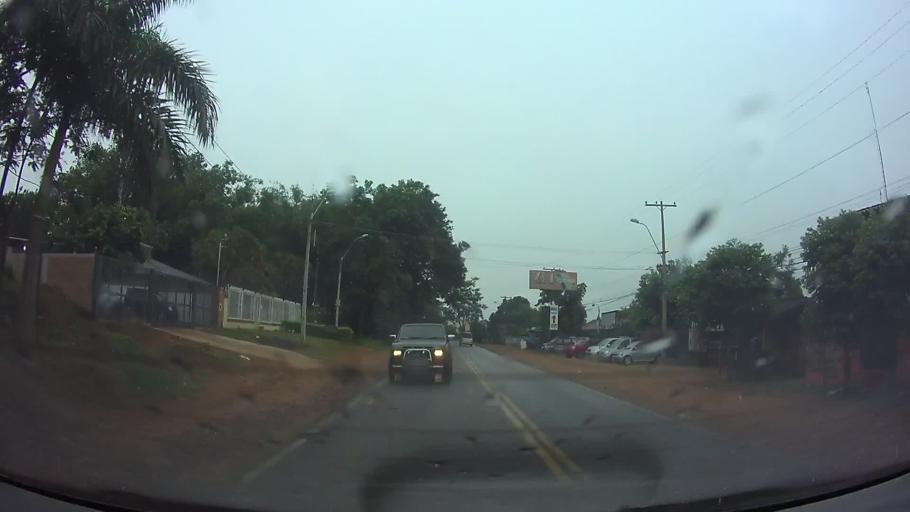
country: PY
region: Central
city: Ita
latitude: -25.5032
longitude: -57.3571
